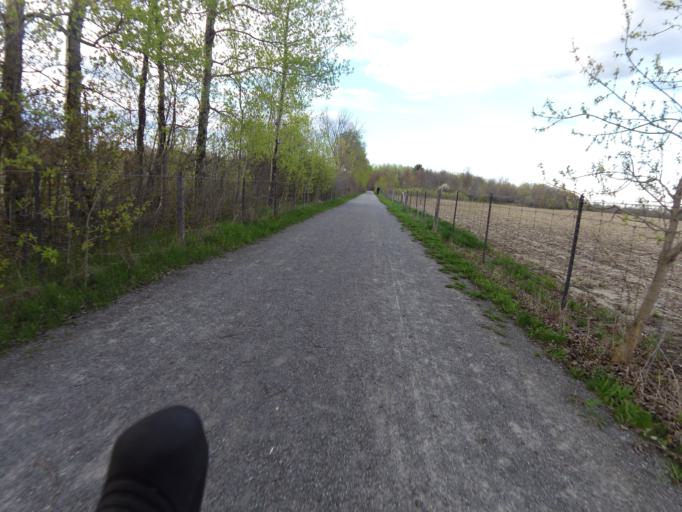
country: CA
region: Ontario
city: Bells Corners
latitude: 45.3117
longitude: -75.7269
